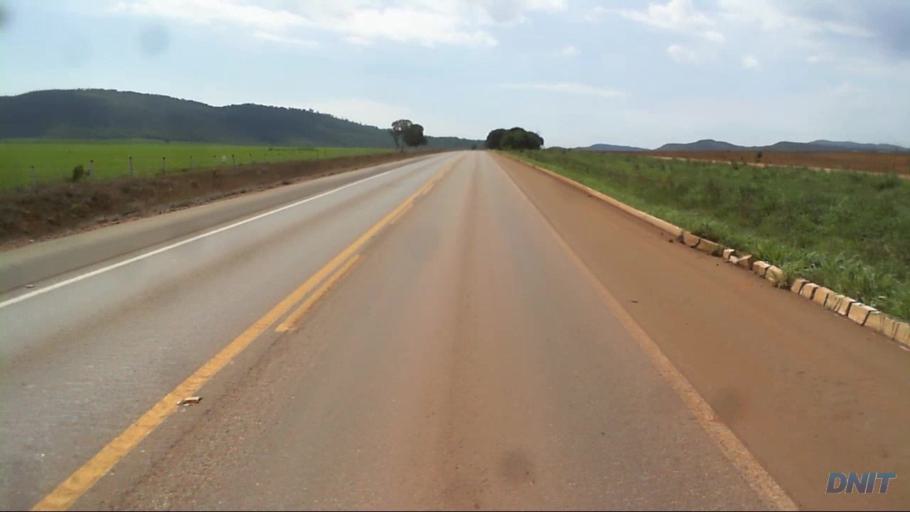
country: BR
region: Goias
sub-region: Barro Alto
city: Barro Alto
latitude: -15.1004
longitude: -48.8510
